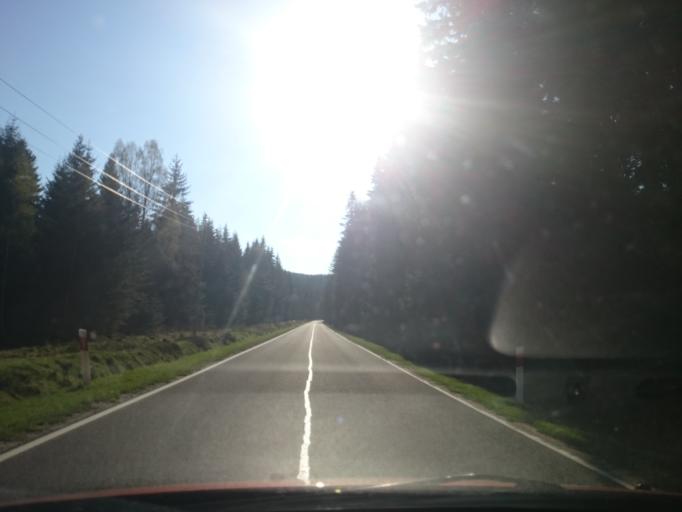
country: PL
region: Lower Silesian Voivodeship
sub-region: Powiat klodzki
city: Duszniki-Zdroj
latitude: 50.3253
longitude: 16.4231
